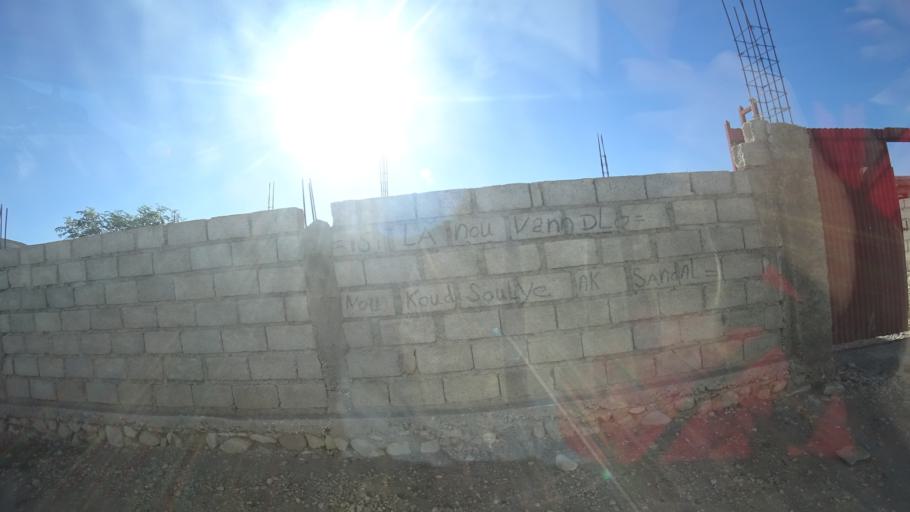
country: HT
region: Ouest
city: Cabaret
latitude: 18.6890
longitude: -72.3198
